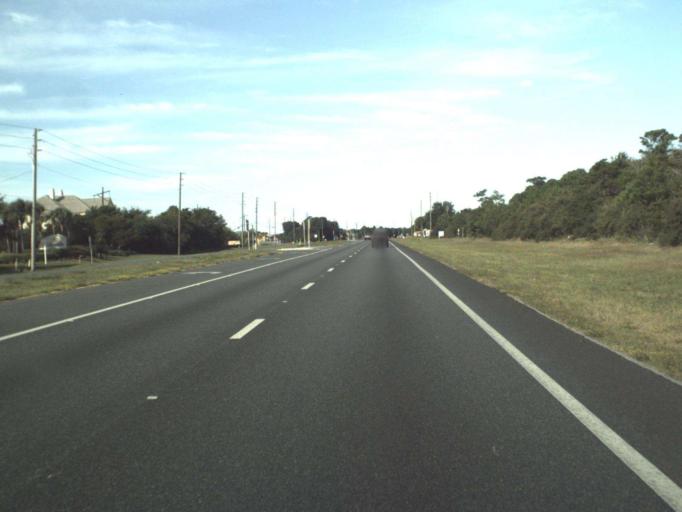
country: US
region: Florida
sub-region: Walton County
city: Miramar Beach
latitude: 30.3854
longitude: -86.3900
